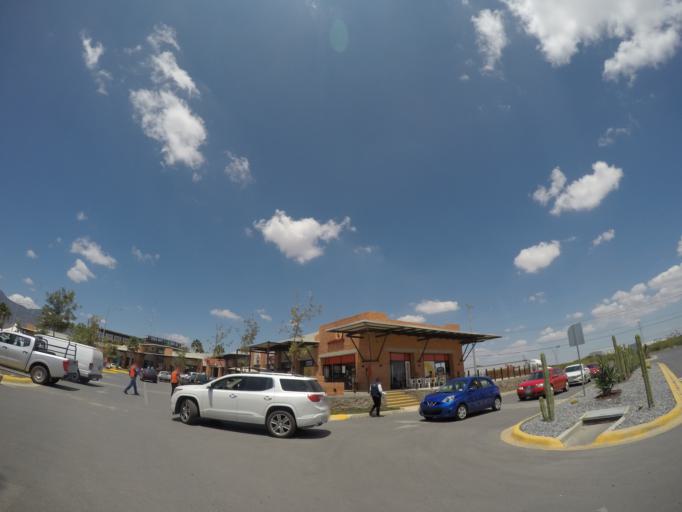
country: MX
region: San Luis Potosi
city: La Pila
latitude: 22.0412
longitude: -100.8926
